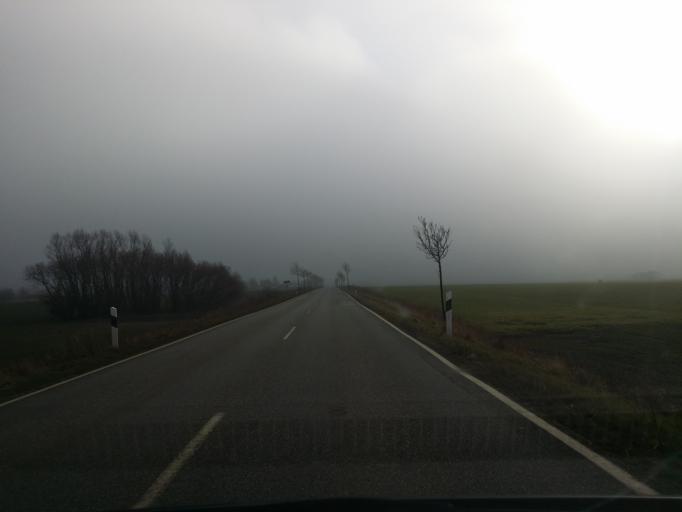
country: DE
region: Schleswig-Holstein
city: Fehmarn
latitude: 54.4343
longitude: 11.1357
